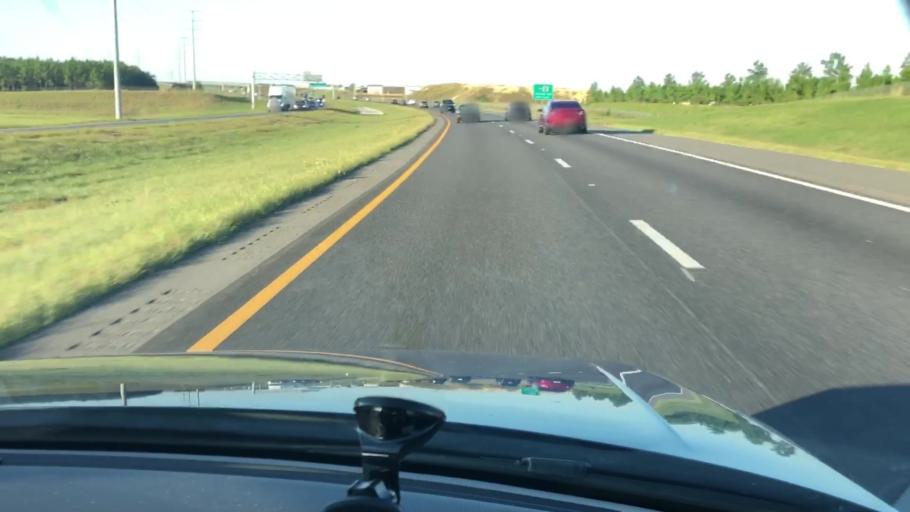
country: US
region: Florida
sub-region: Orange County
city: Oakland
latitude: 28.4643
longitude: -81.6322
